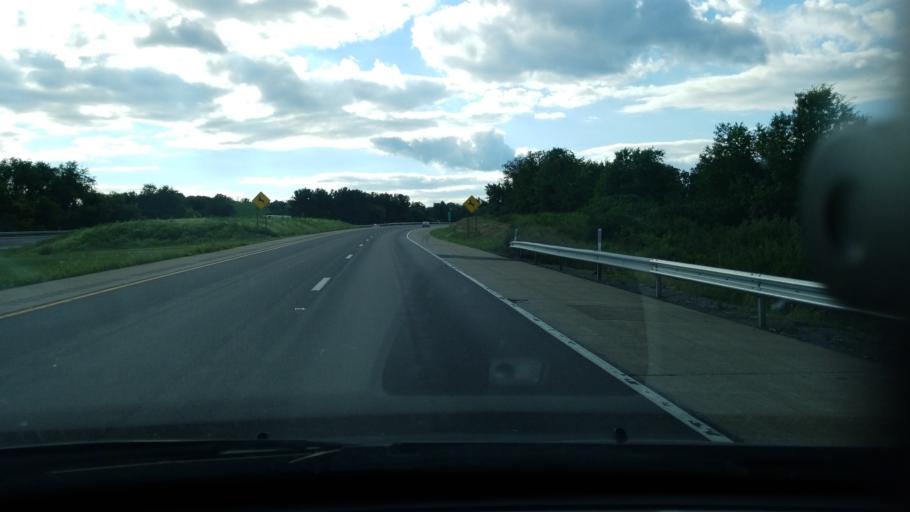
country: US
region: Pennsylvania
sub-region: Northumberland County
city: Milton
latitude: 41.0119
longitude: -76.7815
